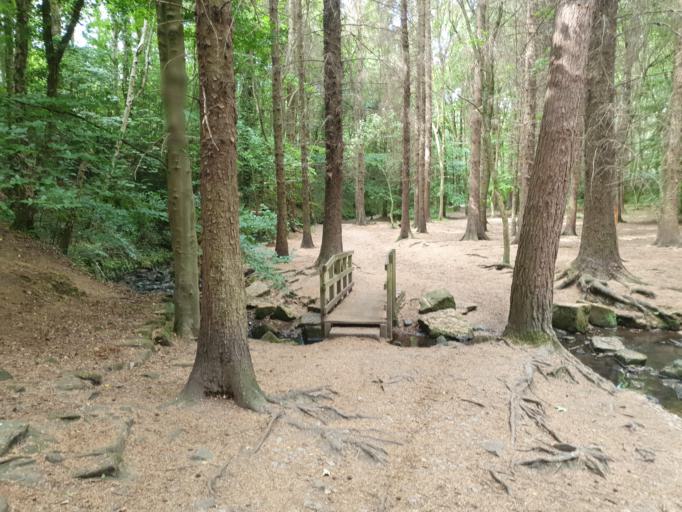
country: GB
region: England
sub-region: City and Borough of Leeds
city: Guiseley
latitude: 53.8626
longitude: -1.7107
